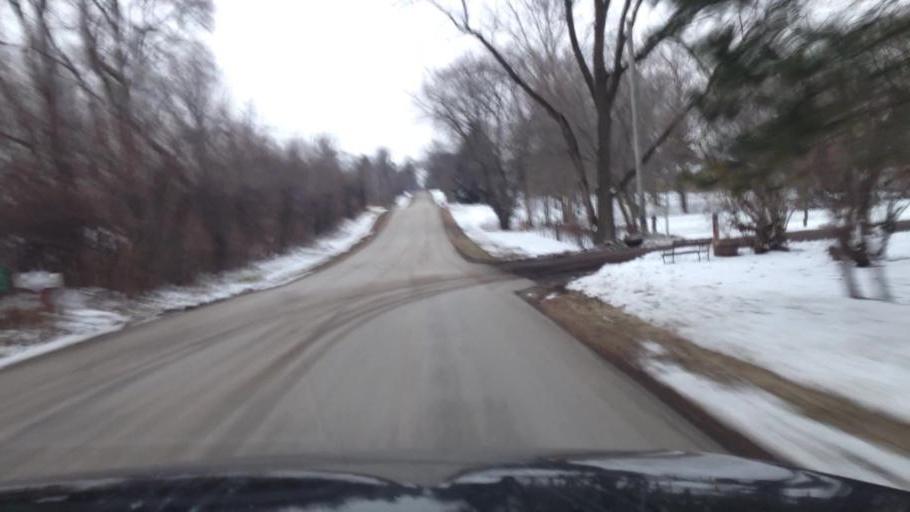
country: US
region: Illinois
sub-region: McHenry County
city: Woodstock
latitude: 42.2711
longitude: -88.4721
